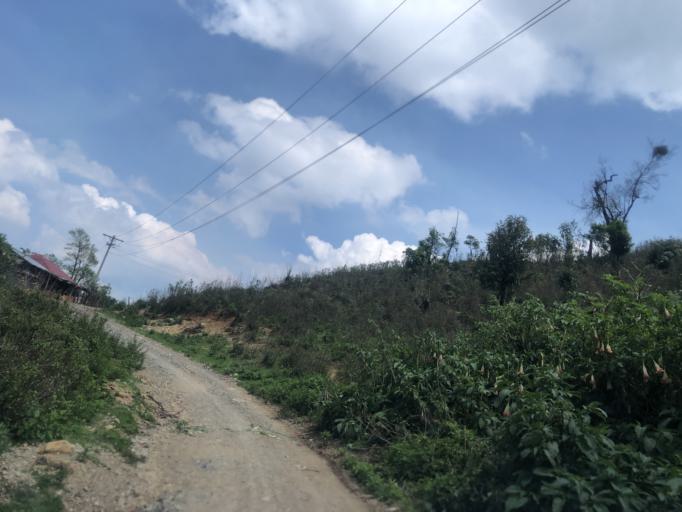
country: LA
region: Phongsali
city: Phongsali
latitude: 21.3908
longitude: 102.1925
